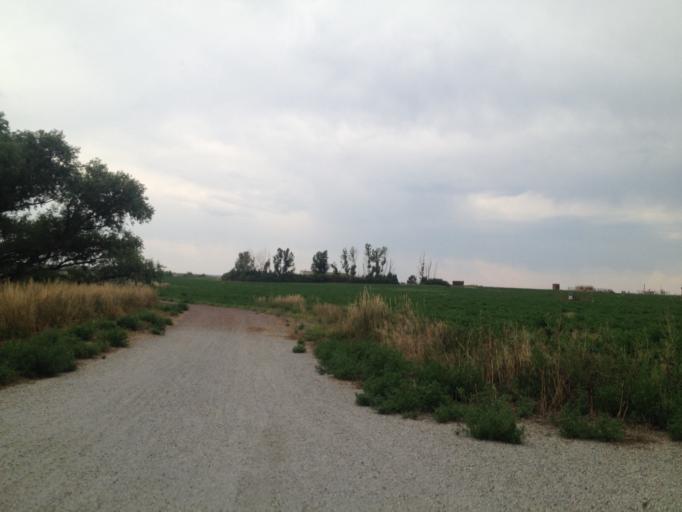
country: US
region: Colorado
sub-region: Boulder County
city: Erie
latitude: 40.0172
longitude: -105.0526
